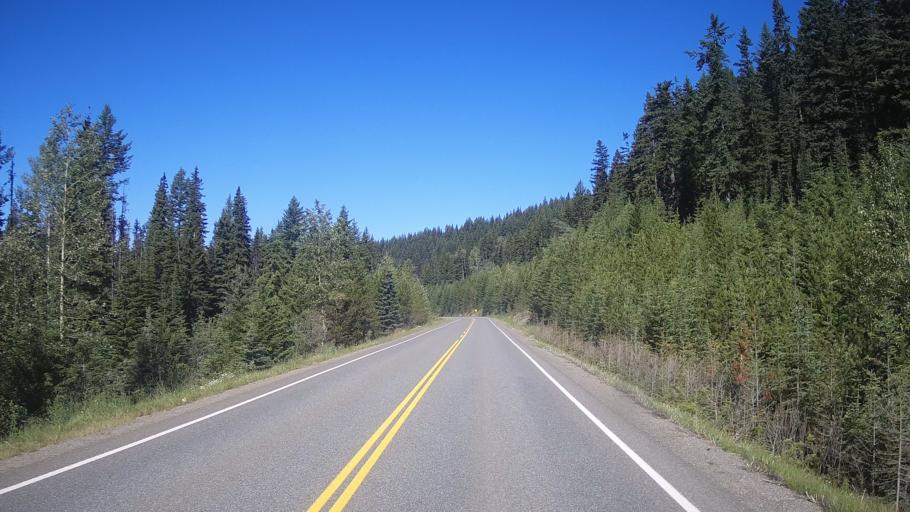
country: CA
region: British Columbia
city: Kamloops
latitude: 51.4982
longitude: -120.4363
